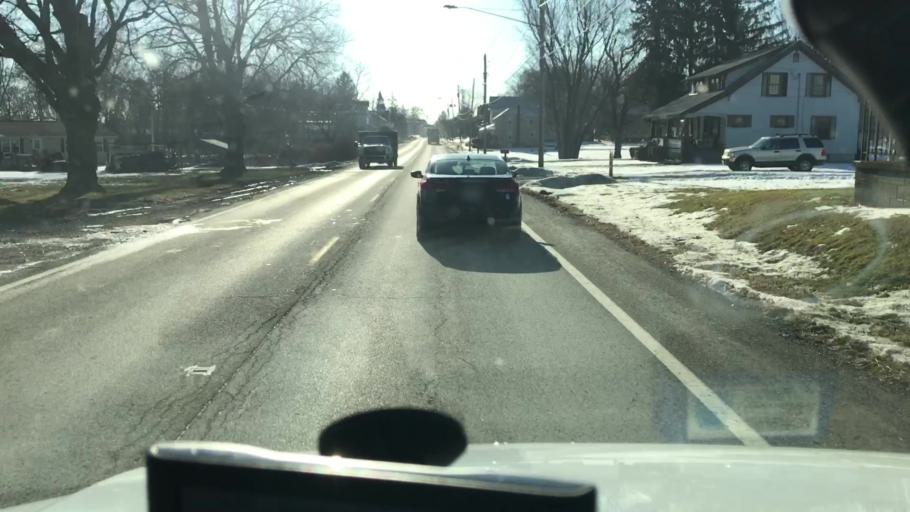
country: US
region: Ohio
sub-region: Mahoning County
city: New Middletown
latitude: 40.9212
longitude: -80.6115
